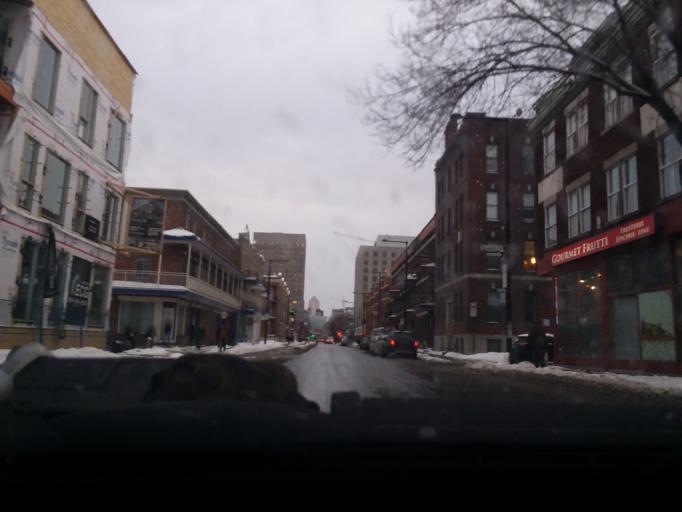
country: CA
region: Quebec
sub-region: Montreal
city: Montreal
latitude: 45.5198
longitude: -73.5571
